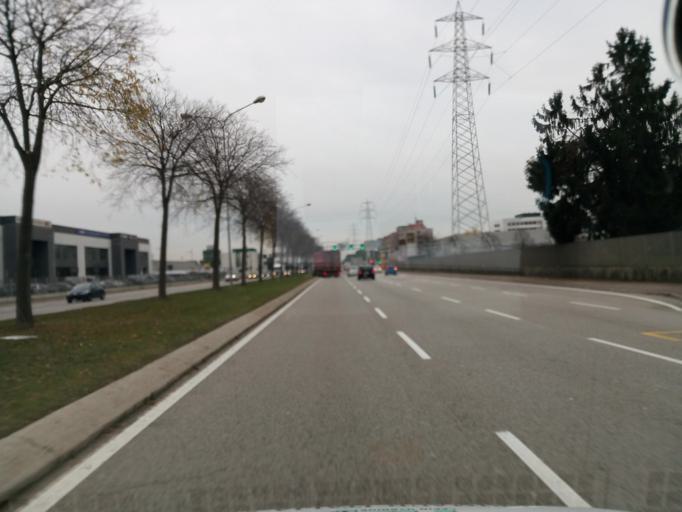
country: IT
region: Veneto
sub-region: Provincia di Padova
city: Noventa
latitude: 45.3952
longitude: 11.9303
